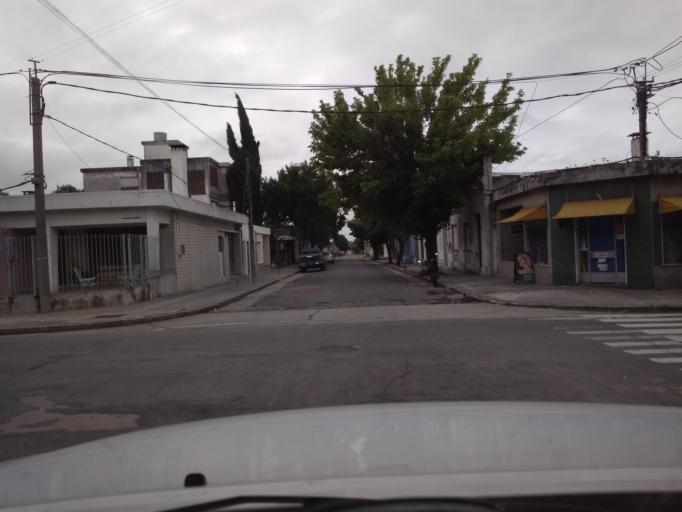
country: UY
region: Florida
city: Florida
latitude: -34.1022
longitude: -56.2139
